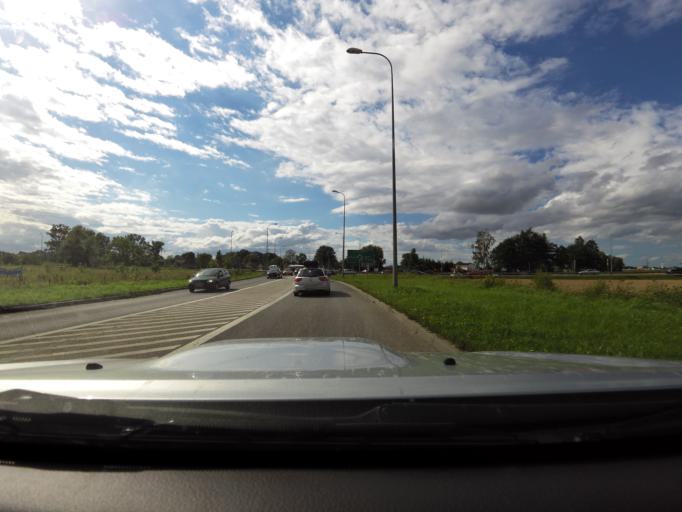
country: PL
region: Pomeranian Voivodeship
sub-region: Powiat gdanski
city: Cedry Wielkie
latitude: 54.2941
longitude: 18.8168
